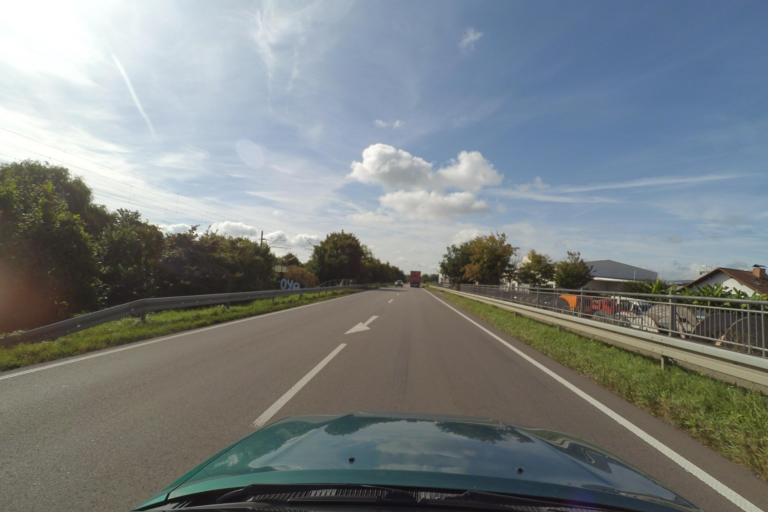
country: DE
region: Baden-Wuerttemberg
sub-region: Freiburg Region
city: Sasbach
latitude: 48.6476
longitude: 8.0813
